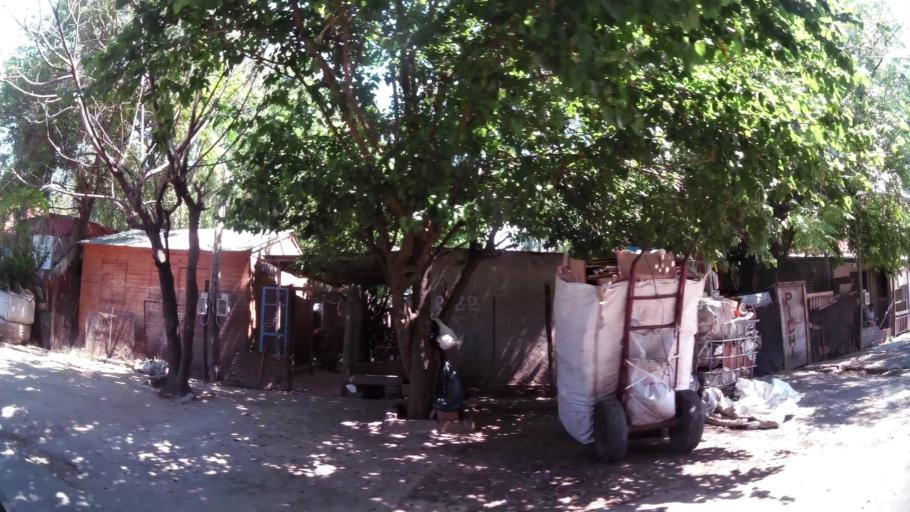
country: AR
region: Buenos Aires
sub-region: Partido de Tigre
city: Tigre
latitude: -34.4747
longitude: -58.5984
